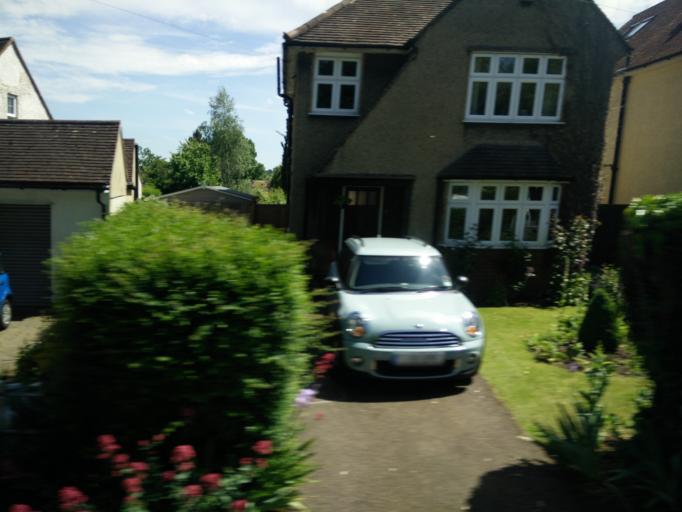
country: GB
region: England
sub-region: Hertfordshire
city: Hitchin
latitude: 51.9458
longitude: -0.2876
